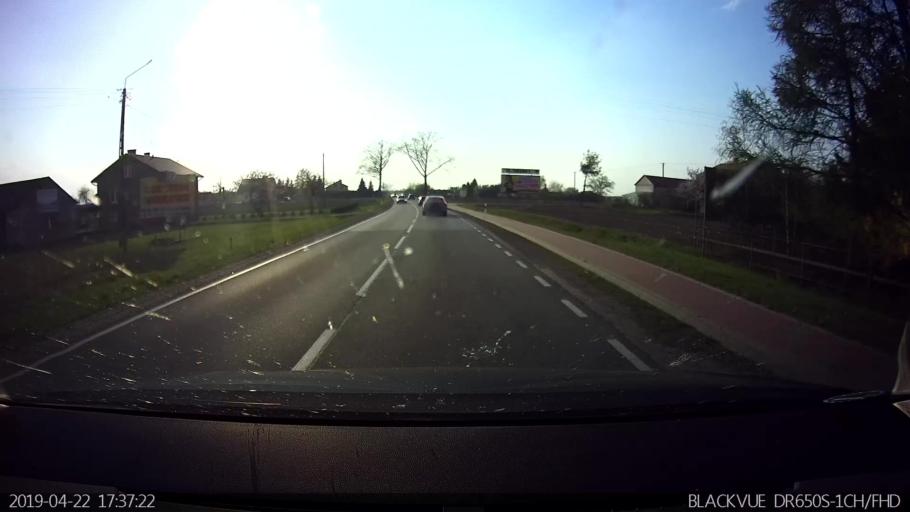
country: PL
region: Masovian Voivodeship
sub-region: Powiat sokolowski
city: Sokolow Podlaski
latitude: 52.4093
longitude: 22.1750
